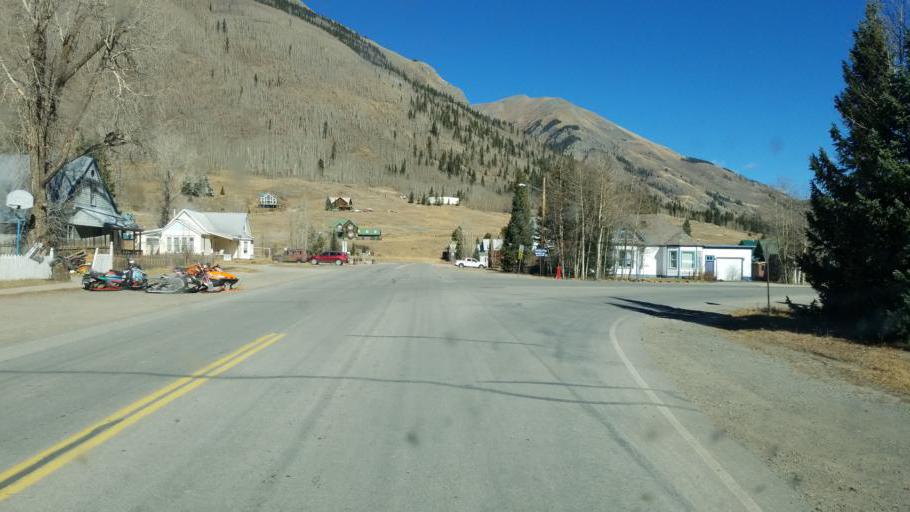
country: US
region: Colorado
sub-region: San Juan County
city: Silverton
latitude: 37.8154
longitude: -107.6609
